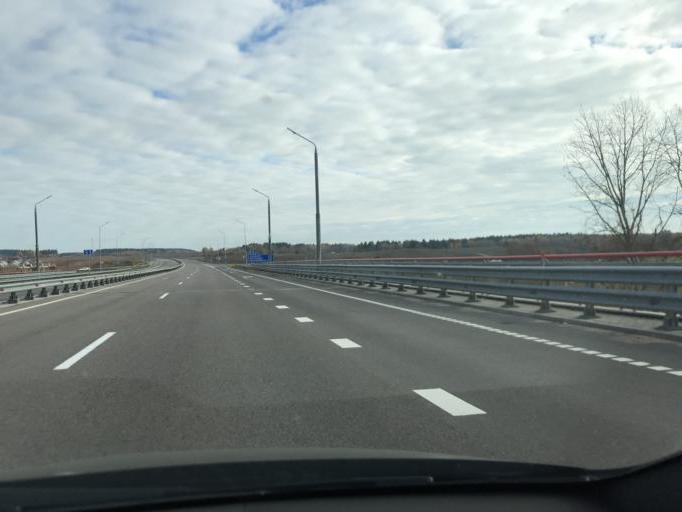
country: BY
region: Minsk
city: Pyatryshki
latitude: 54.0564
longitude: 27.2129
